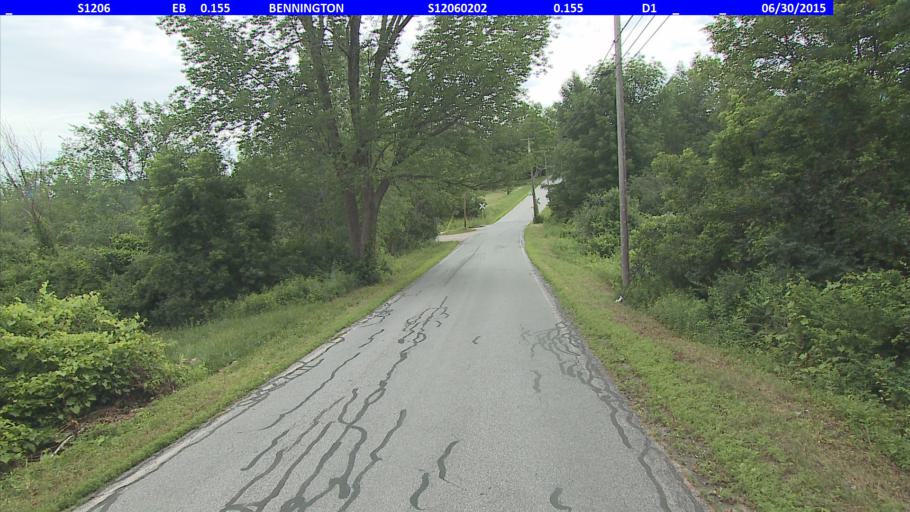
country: US
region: Vermont
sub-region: Bennington County
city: North Bennington
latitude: 42.9272
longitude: -73.2247
